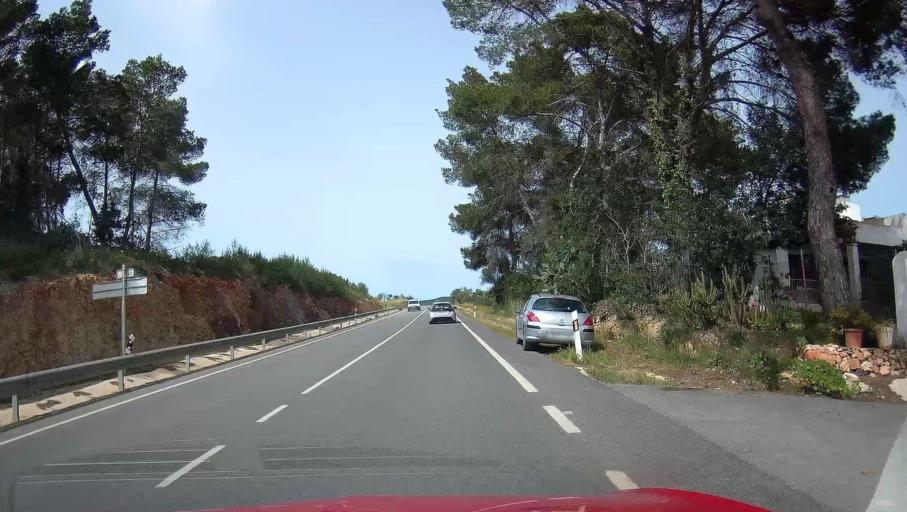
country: ES
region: Balearic Islands
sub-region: Illes Balears
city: Sant Joan de Labritja
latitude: 39.0350
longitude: 1.4910
